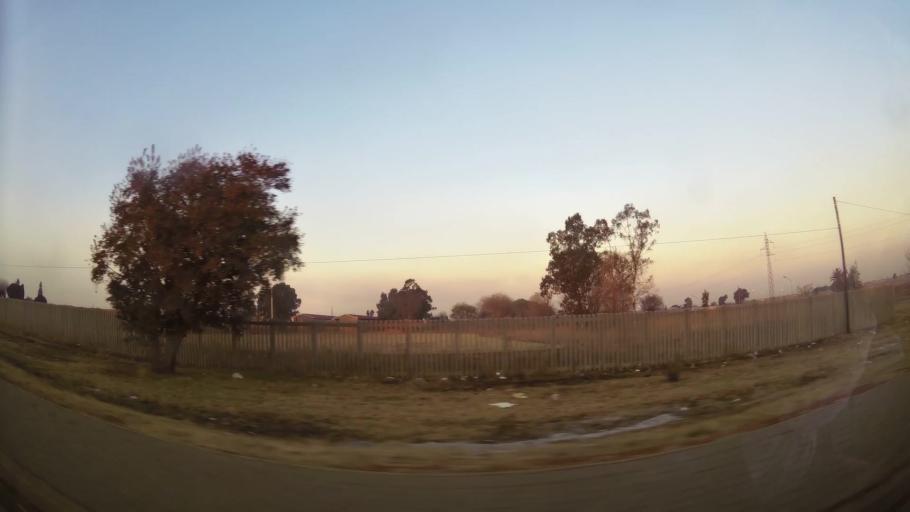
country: ZA
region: Gauteng
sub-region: Ekurhuleni Metropolitan Municipality
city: Springs
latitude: -26.3026
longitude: 28.4074
